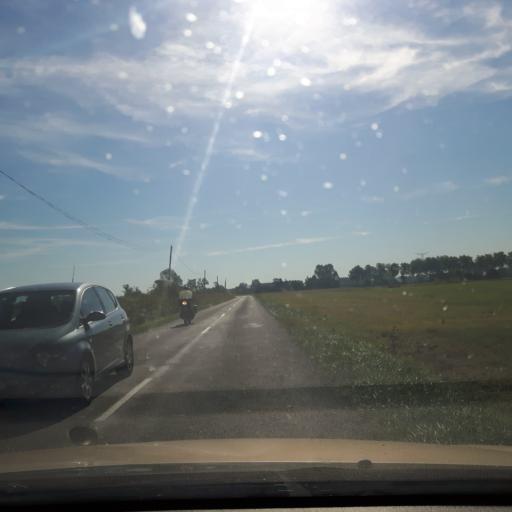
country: FR
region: Midi-Pyrenees
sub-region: Departement de la Haute-Garonne
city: Cepet
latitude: 43.7587
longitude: 1.4297
